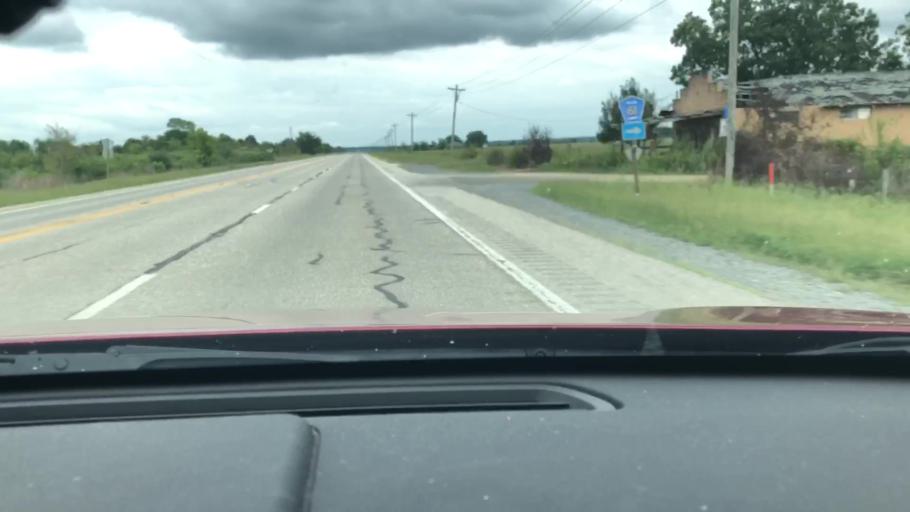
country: US
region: Arkansas
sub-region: Lafayette County
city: Lewisville
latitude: 33.4126
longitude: -93.7963
